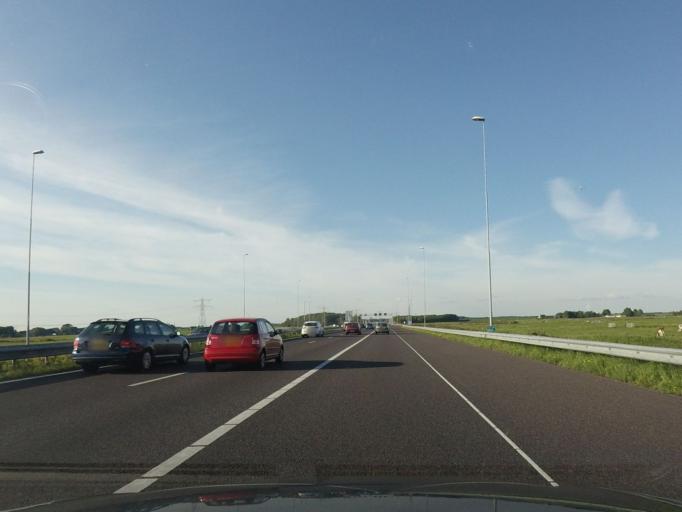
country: NL
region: North Holland
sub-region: Gemeente Haarlem
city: Haarlem
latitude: 52.3944
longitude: 4.7059
